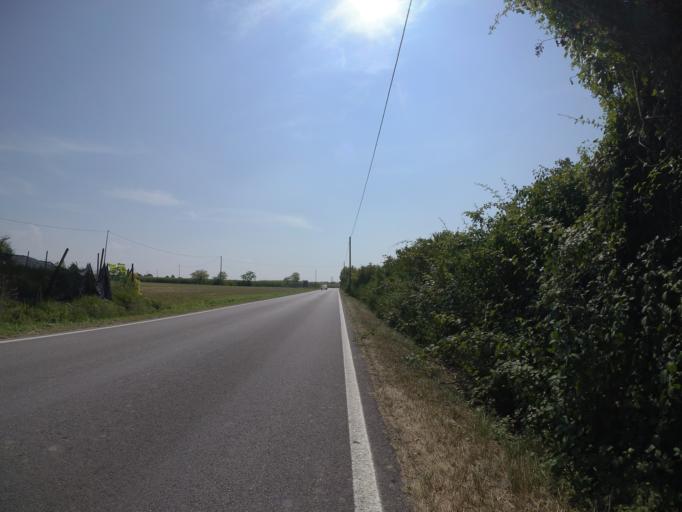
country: IT
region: Friuli Venezia Giulia
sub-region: Provincia di Udine
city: Pocenia
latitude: 45.8597
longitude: 13.0888
